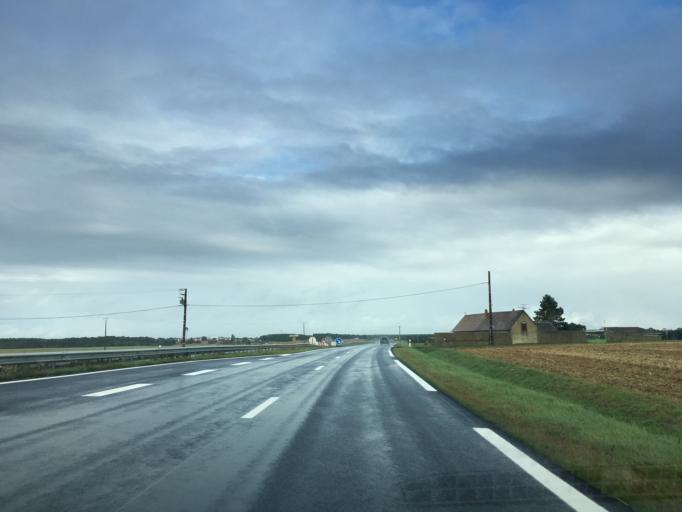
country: FR
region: Haute-Normandie
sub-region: Departement de l'Eure
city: Tillieres-sur-Avre
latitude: 48.7485
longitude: 1.0120
